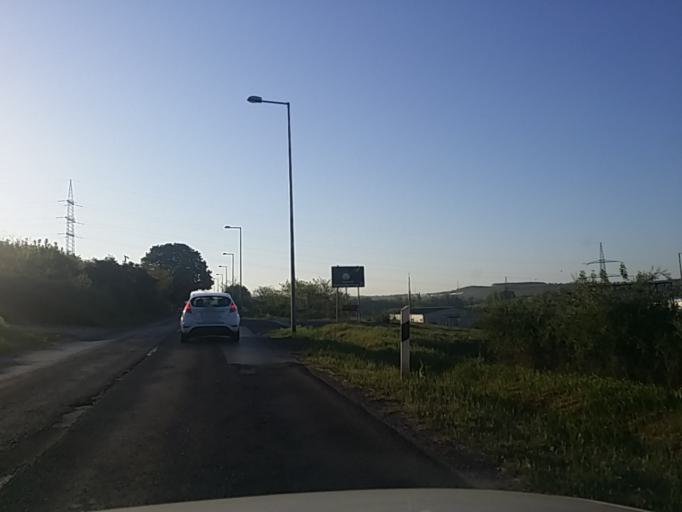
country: HU
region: Pest
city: Mogyorod
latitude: 47.5994
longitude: 19.2229
